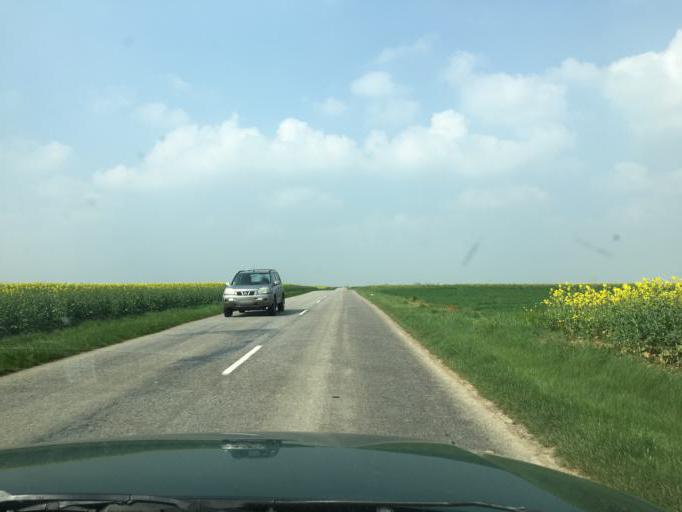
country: FR
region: Centre
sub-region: Departement du Loiret
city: Beaugency
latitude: 47.8318
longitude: 1.5660
